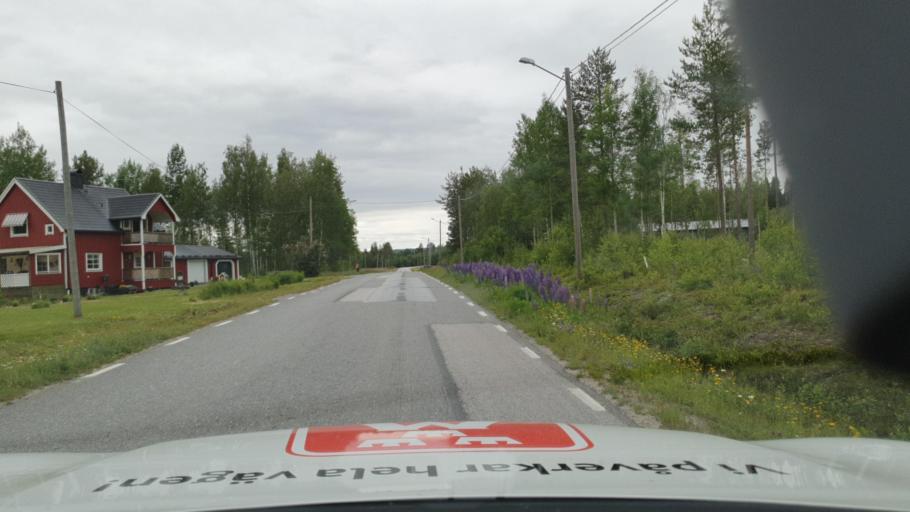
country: SE
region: Vaesterbotten
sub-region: Nordmalings Kommun
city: Nordmaling
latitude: 63.5285
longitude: 19.4097
